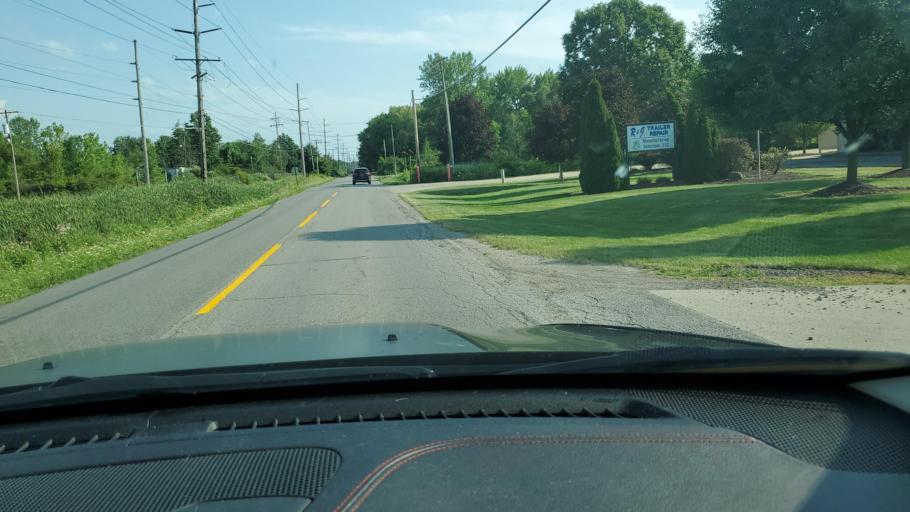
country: US
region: Ohio
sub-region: Mahoning County
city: Boardman
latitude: 41.0032
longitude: -80.6533
